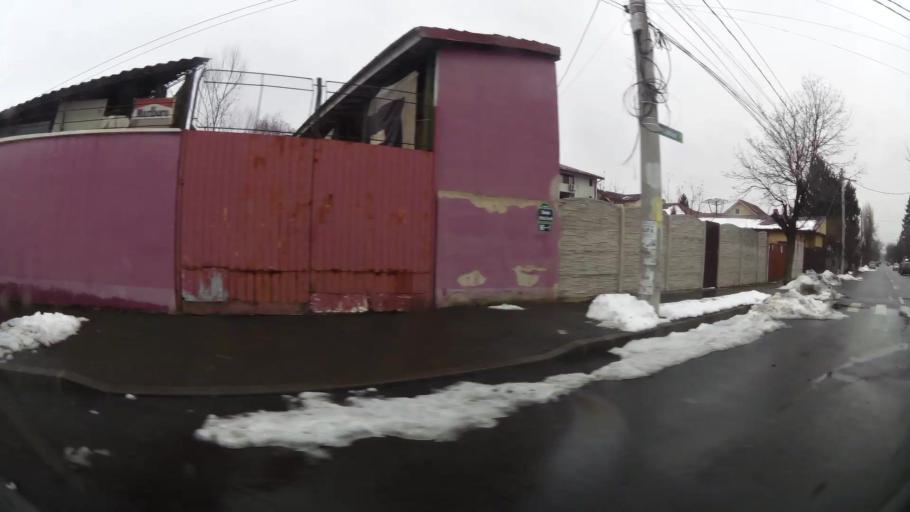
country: RO
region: Ilfov
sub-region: Comuna Mogosoaia
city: Mogosoaia
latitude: 44.5022
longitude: 26.0242
